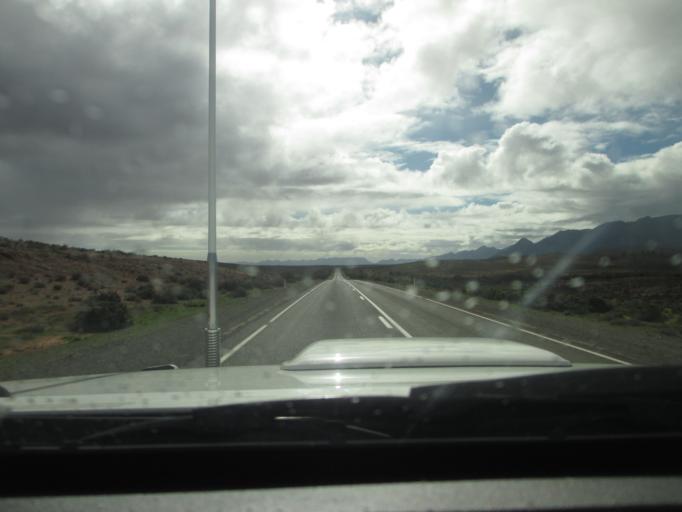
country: AU
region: South Australia
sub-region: Flinders Ranges
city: Quorn
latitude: -31.5840
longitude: 138.4169
